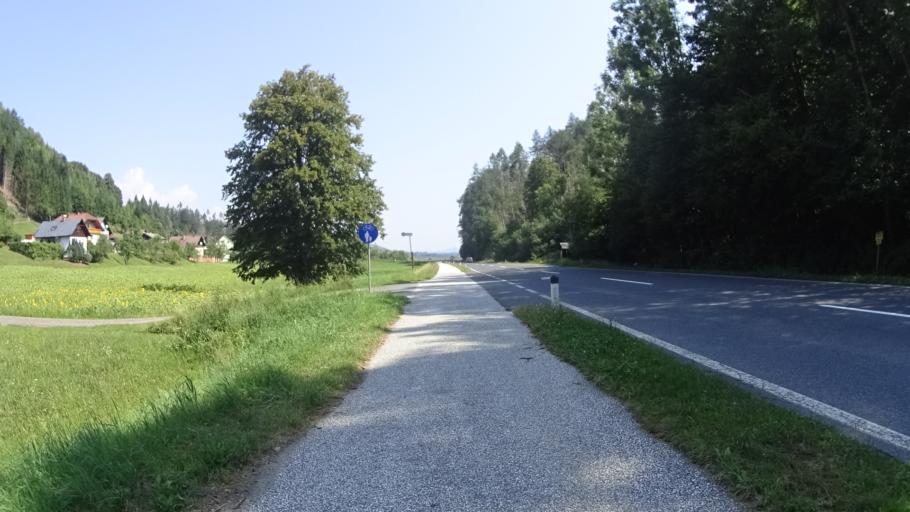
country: AT
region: Carinthia
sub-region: Politischer Bezirk Volkermarkt
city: Sittersdorf
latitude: 46.5529
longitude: 14.6113
